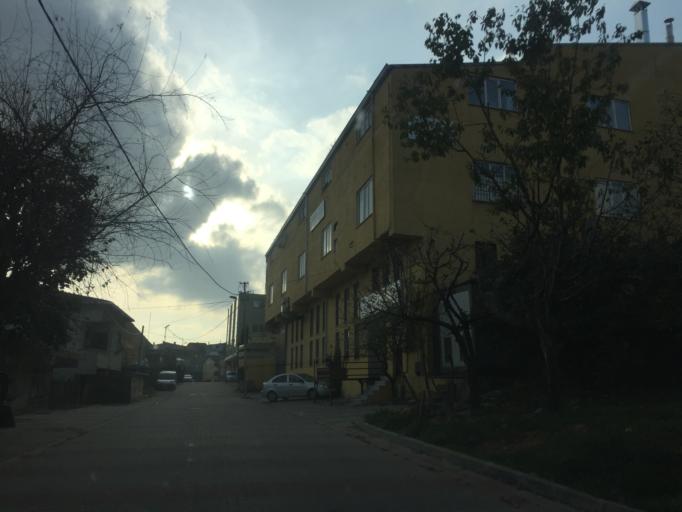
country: TR
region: Istanbul
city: Sultanbeyli
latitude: 40.9480
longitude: 29.2962
